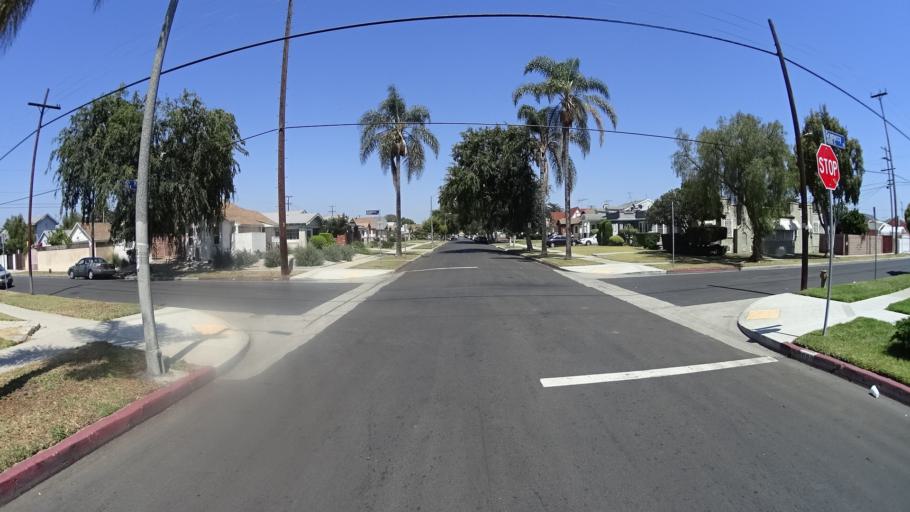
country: US
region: California
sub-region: Los Angeles County
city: View Park-Windsor Hills
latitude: 34.0064
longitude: -118.3139
